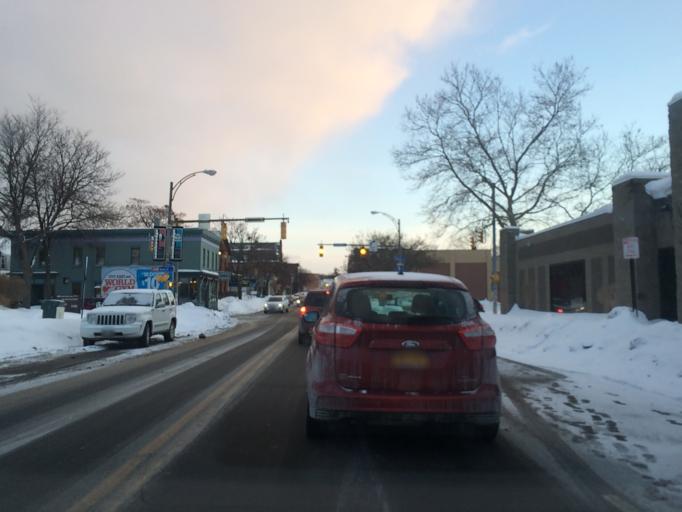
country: US
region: New York
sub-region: Monroe County
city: Rochester
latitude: 43.1444
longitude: -77.6050
